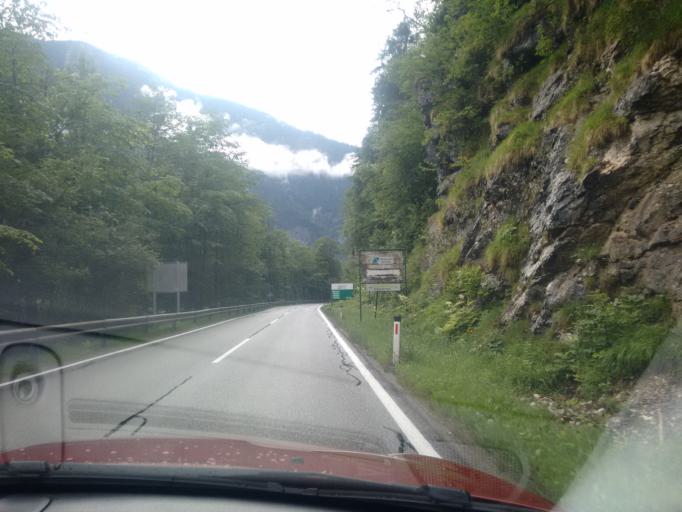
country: AT
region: Upper Austria
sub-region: Politischer Bezirk Gmunden
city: Bad Goisern
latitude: 47.5900
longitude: 13.6542
